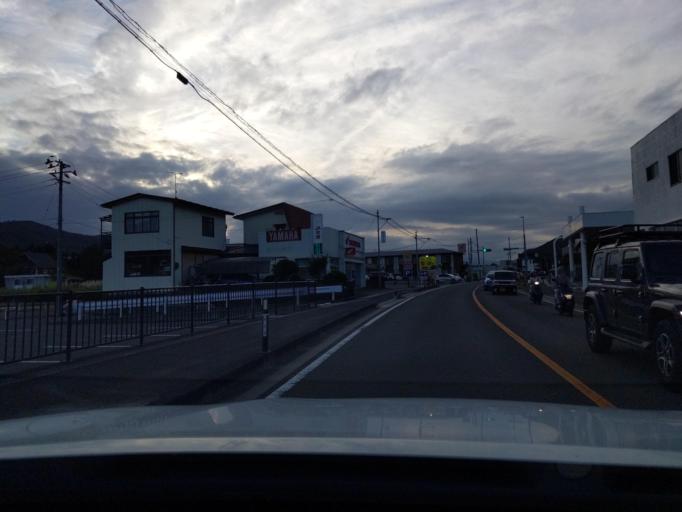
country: JP
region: Miyagi
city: Sendai
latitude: 38.2644
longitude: 140.8190
